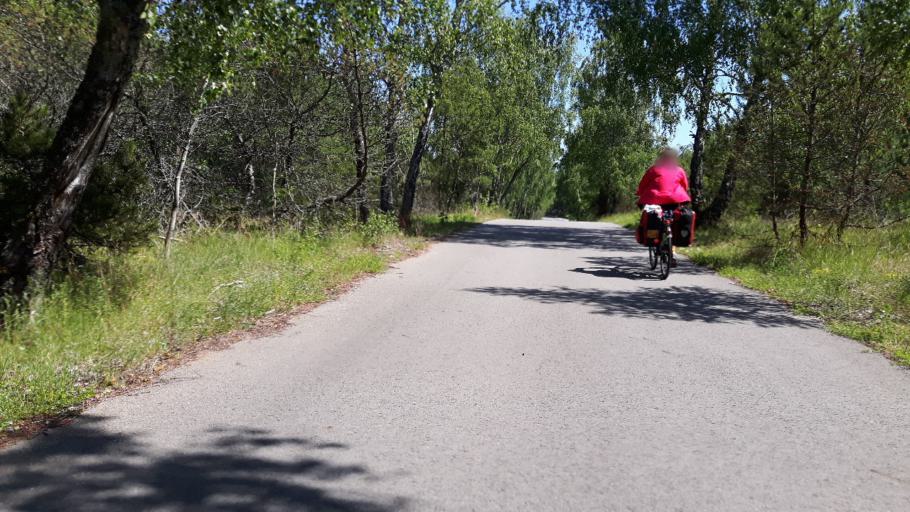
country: LT
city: Neringa
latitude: 55.4113
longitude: 21.0886
